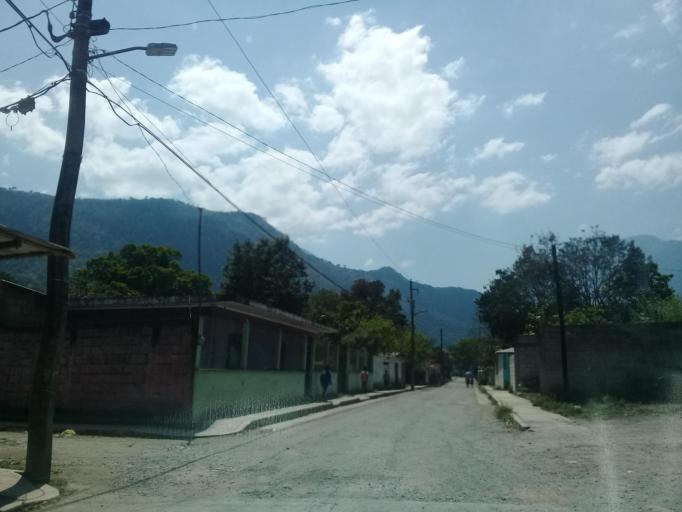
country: MX
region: Veracruz
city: Jalapilla
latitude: 18.8108
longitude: -97.0687
